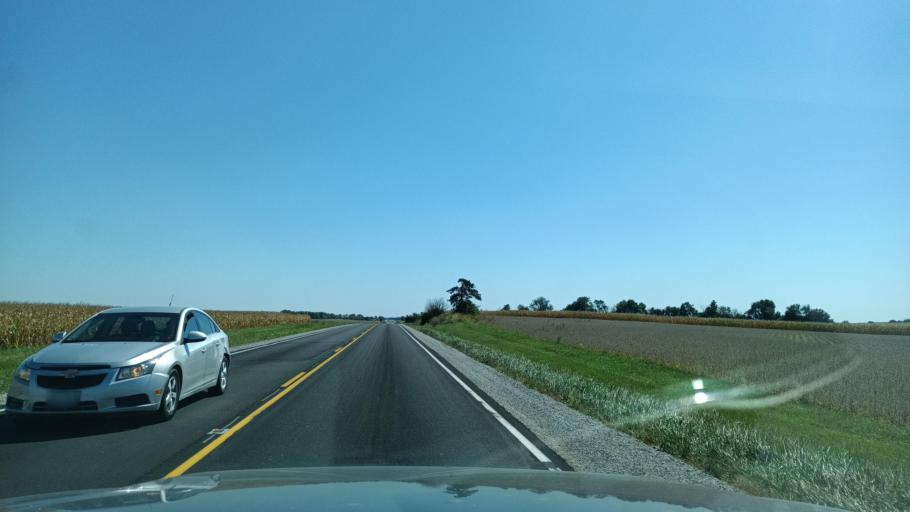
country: US
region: Illinois
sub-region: McLean County
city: Twin Grove
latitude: 40.5553
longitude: -89.0766
